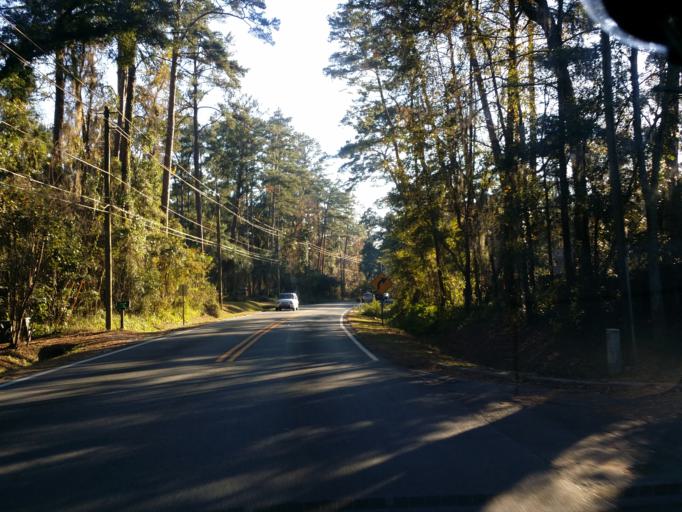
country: US
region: Florida
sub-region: Leon County
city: Tallahassee
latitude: 30.4238
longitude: -84.2621
